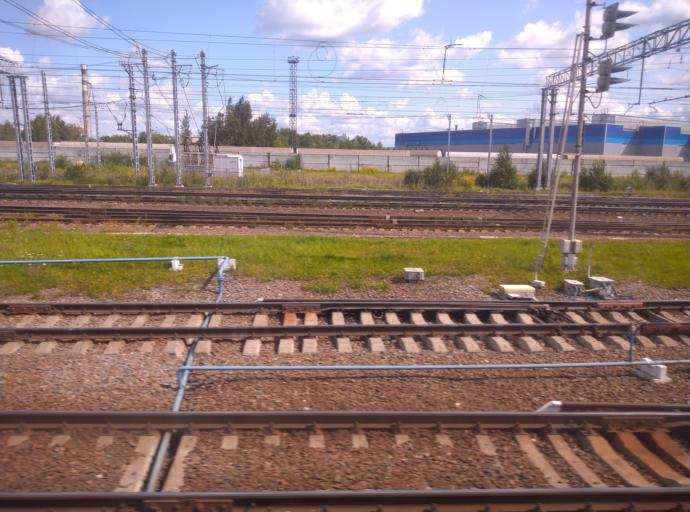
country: RU
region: St.-Petersburg
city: Obukhovo
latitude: 59.8506
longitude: 30.4517
